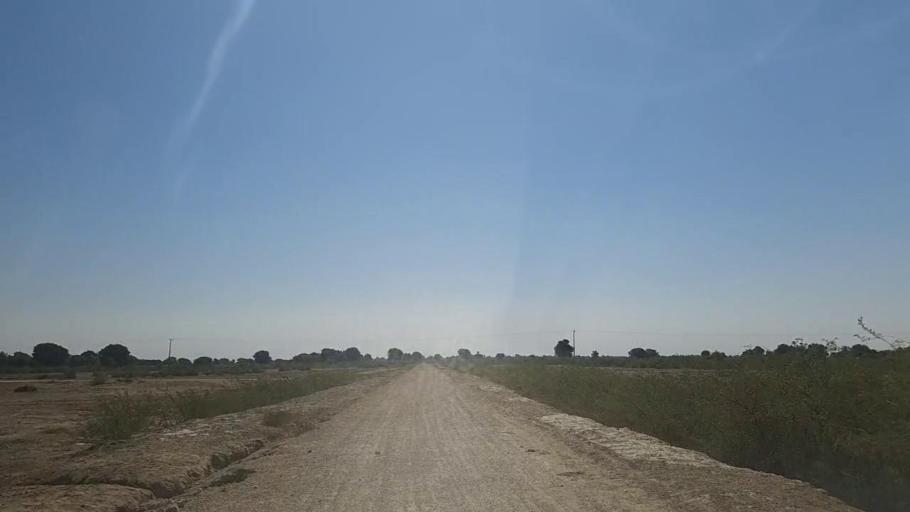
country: PK
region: Sindh
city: Dhoro Naro
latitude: 25.3570
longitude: 69.5322
